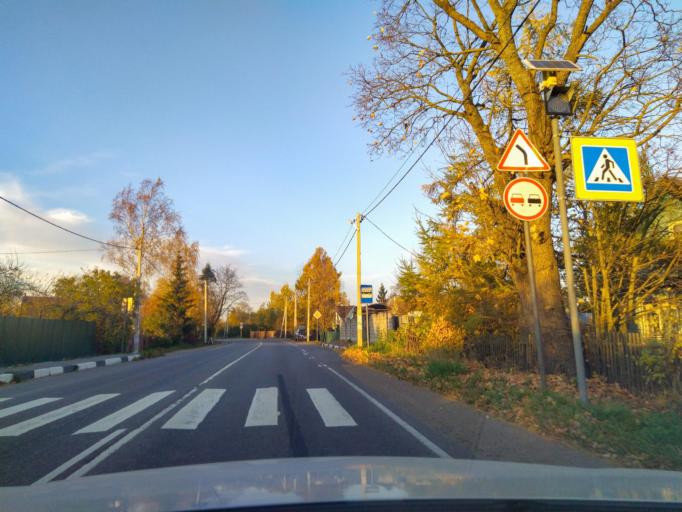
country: RU
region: Leningrad
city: Gatchina
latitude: 59.5021
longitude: 30.1689
